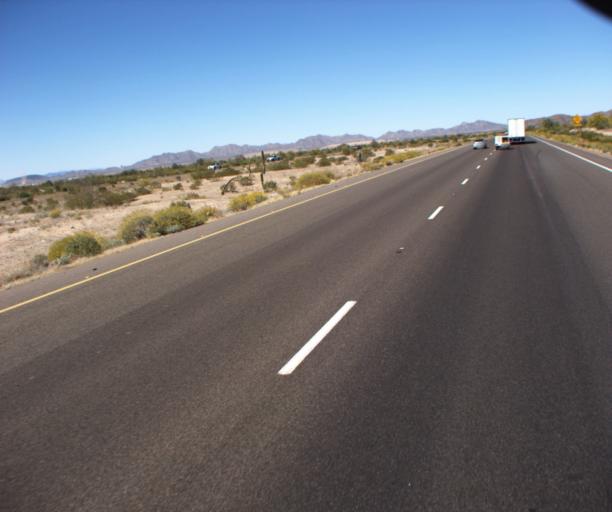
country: US
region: Arizona
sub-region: Maricopa County
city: Gila Bend
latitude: 33.1328
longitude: -112.6501
